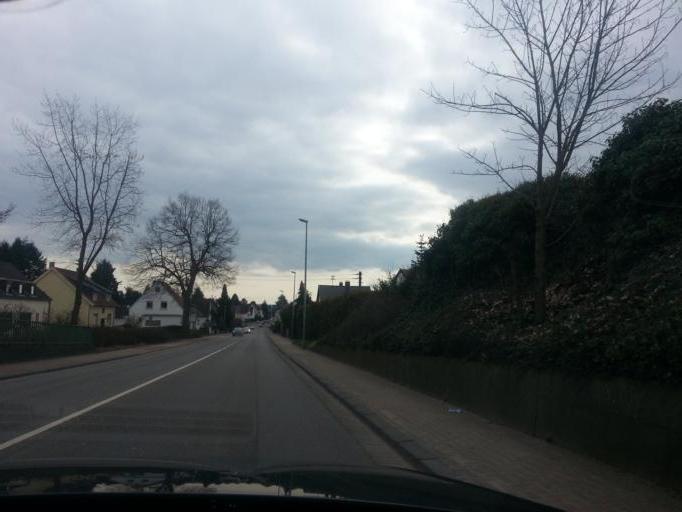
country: DE
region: Saarland
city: Bexbach
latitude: 49.3555
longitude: 7.2653
